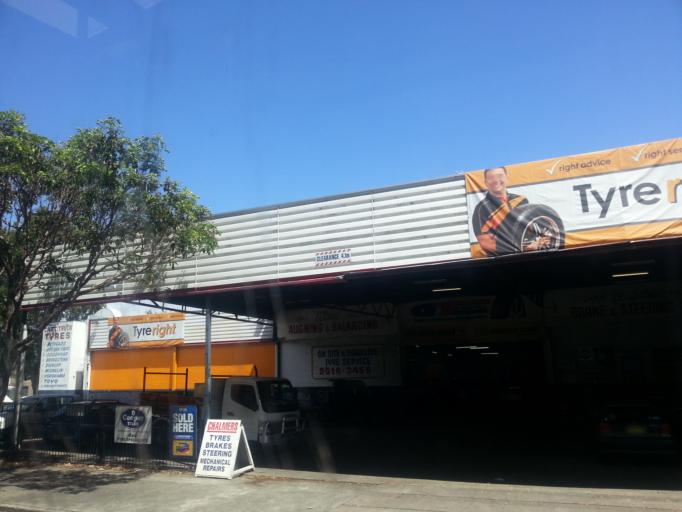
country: AU
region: New South Wales
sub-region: City of Sydney
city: Alexandria
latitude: -33.9058
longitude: 151.1921
